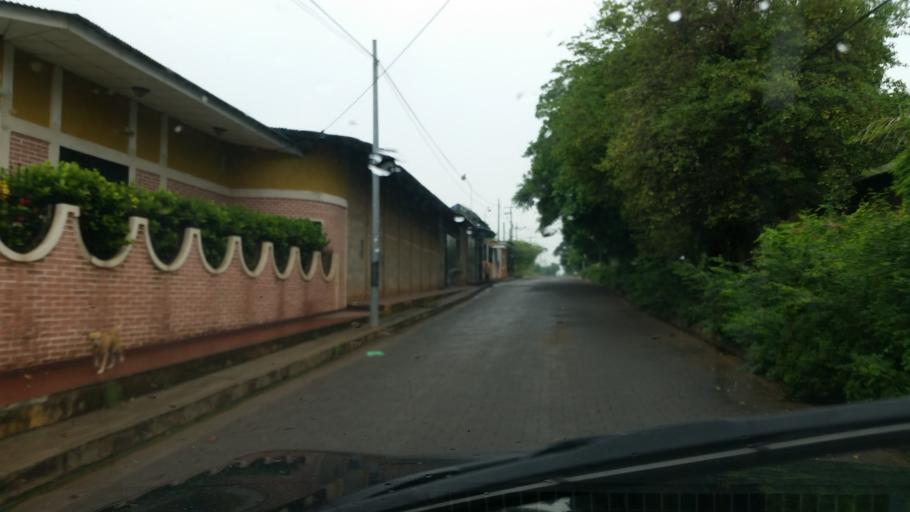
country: NI
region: Granada
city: Granada
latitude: 11.9341
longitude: -85.9640
